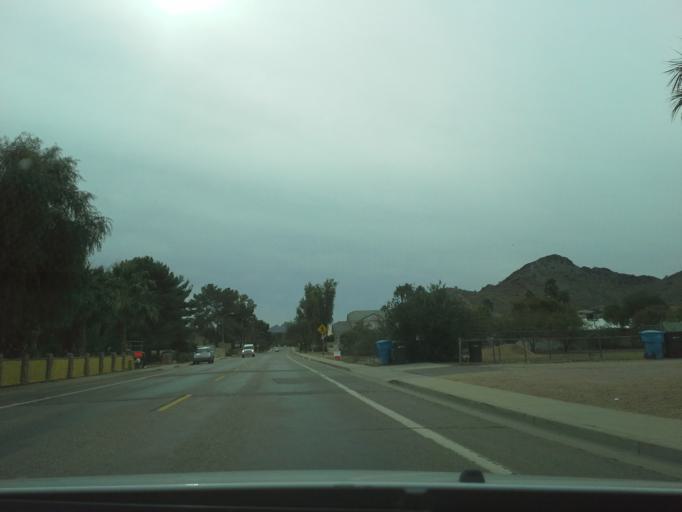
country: US
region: Arizona
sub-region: Maricopa County
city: Paradise Valley
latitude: 33.6238
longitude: -112.0221
